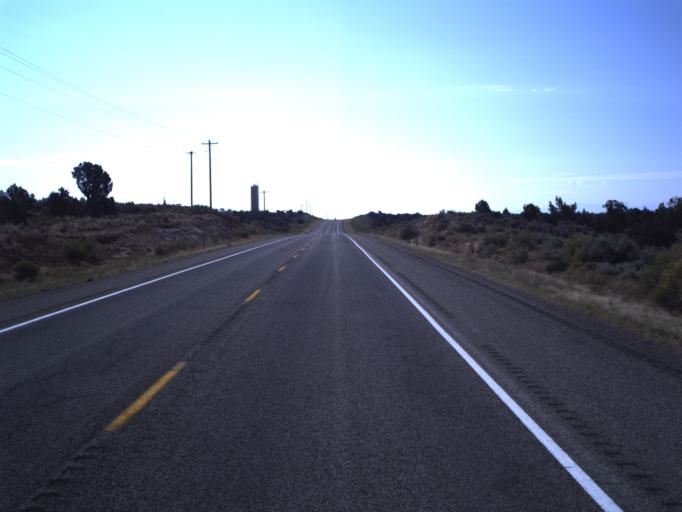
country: US
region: Utah
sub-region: San Juan County
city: Blanding
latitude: 37.4867
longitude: -109.4754
